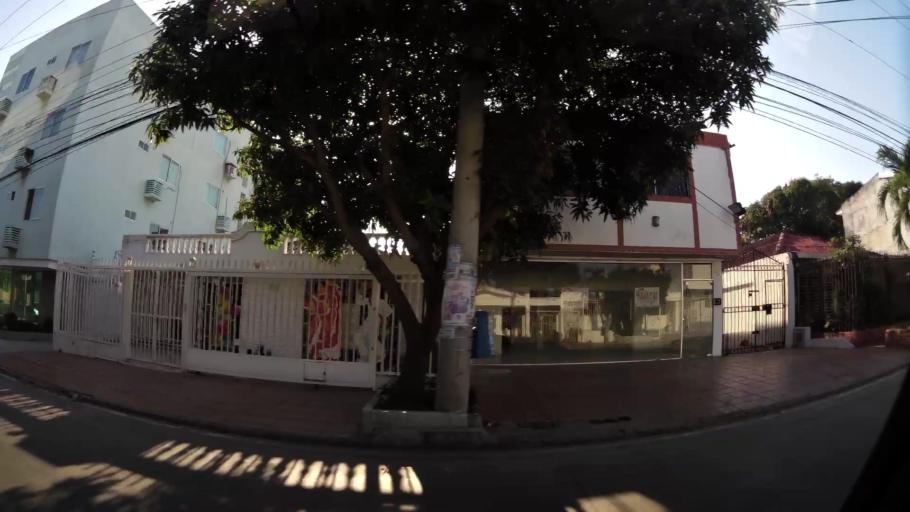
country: CO
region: Atlantico
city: Barranquilla
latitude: 11.0098
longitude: -74.7978
